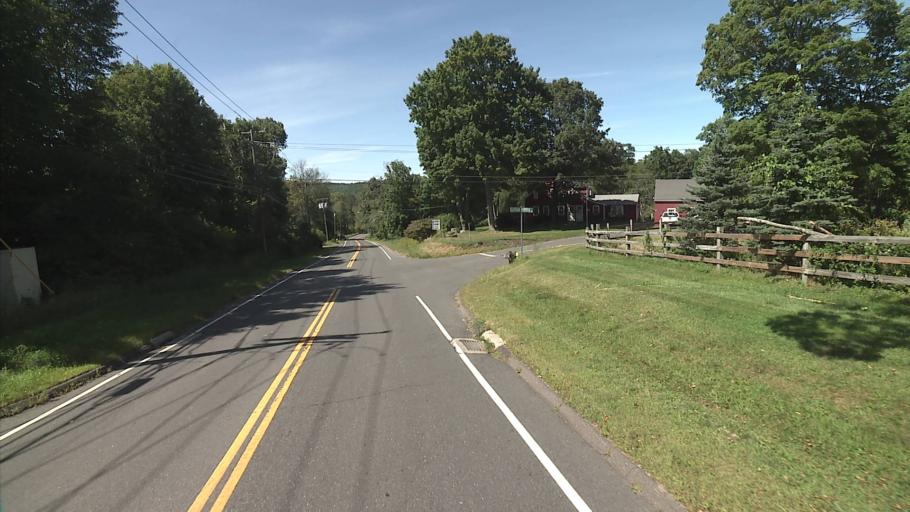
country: US
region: Connecticut
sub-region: New Haven County
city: Oxford
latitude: 41.4202
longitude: -73.1512
